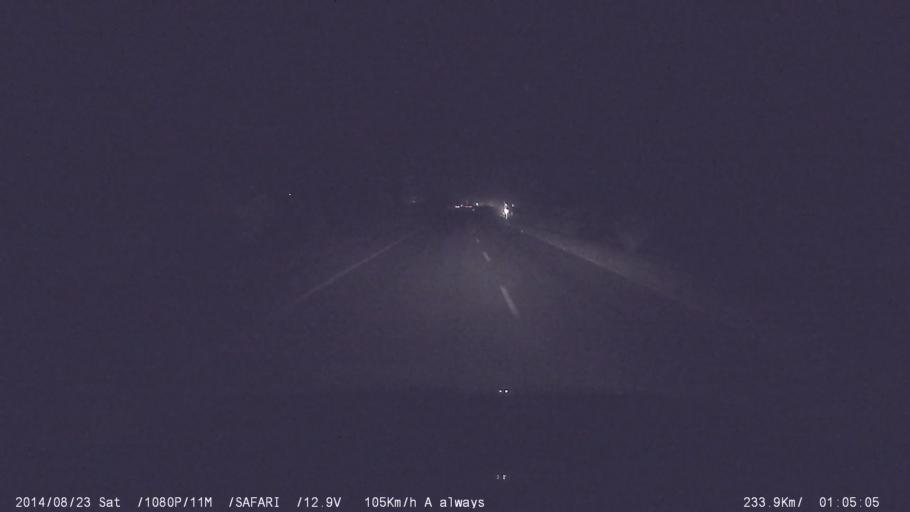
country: IN
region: Tamil Nadu
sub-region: Vellore
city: Walajapet
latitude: 12.9023
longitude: 79.4296
